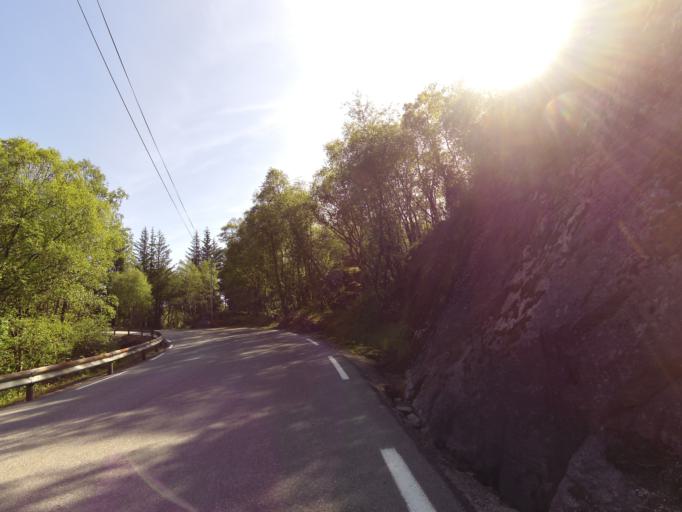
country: NO
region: Rogaland
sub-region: Sokndal
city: Hauge i Dalane
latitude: 58.3397
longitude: 6.3487
